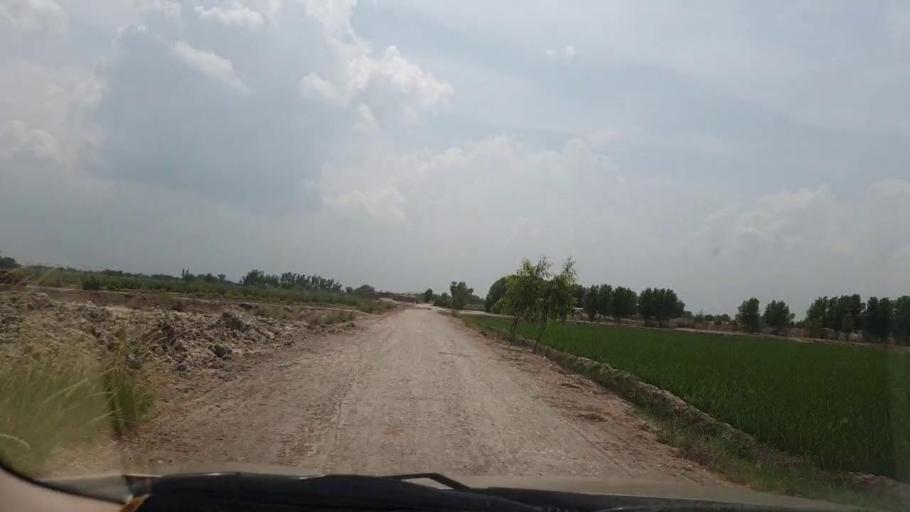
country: PK
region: Sindh
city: Larkana
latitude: 27.6177
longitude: 68.1548
